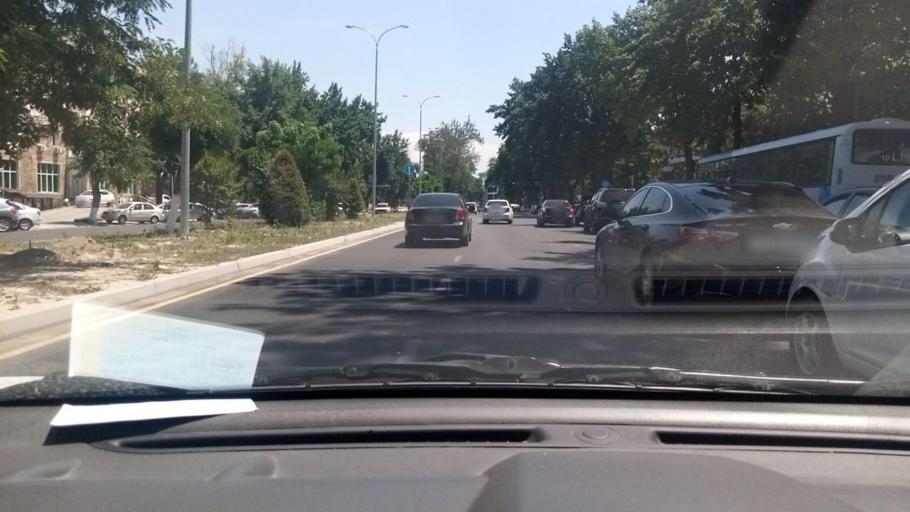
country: UZ
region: Toshkent Shahri
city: Tashkent
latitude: 41.2912
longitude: 69.1999
